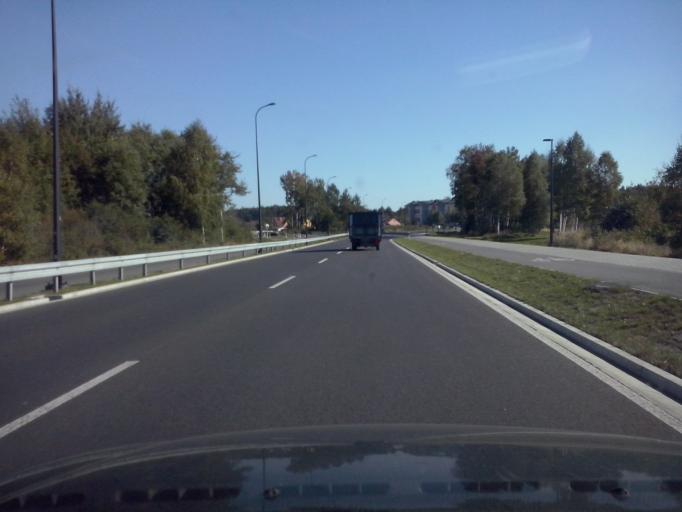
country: PL
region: Lublin Voivodeship
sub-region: Powiat bilgorajski
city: Bilgoraj
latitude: 50.5499
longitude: 22.7344
